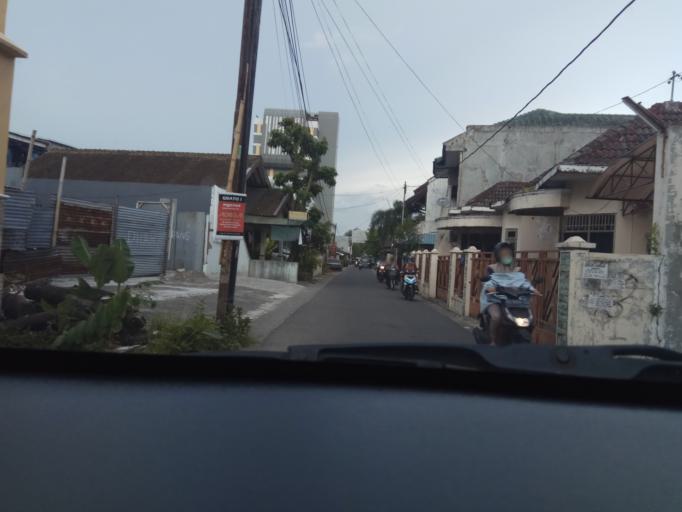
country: ID
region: Daerah Istimewa Yogyakarta
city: Depok
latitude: -7.7621
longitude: 110.3965
